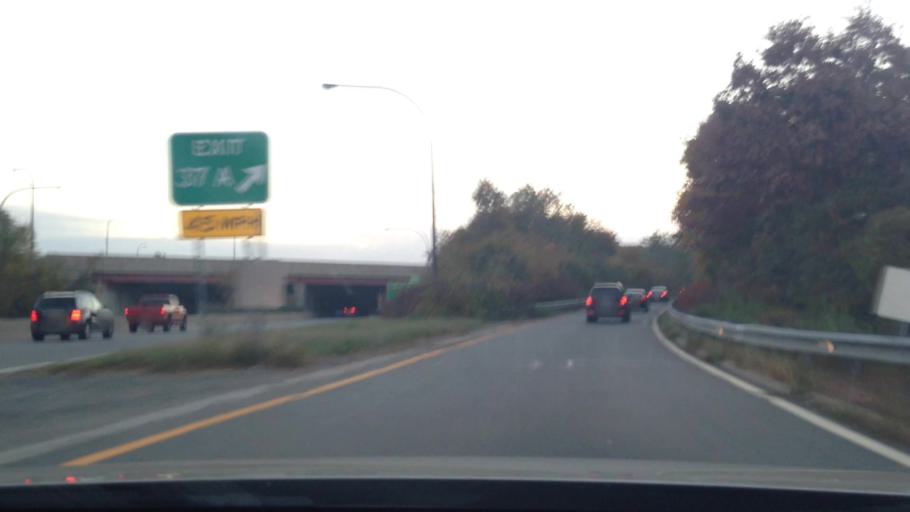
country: US
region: New York
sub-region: Nassau County
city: Plainview
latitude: 40.7969
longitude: -73.4772
